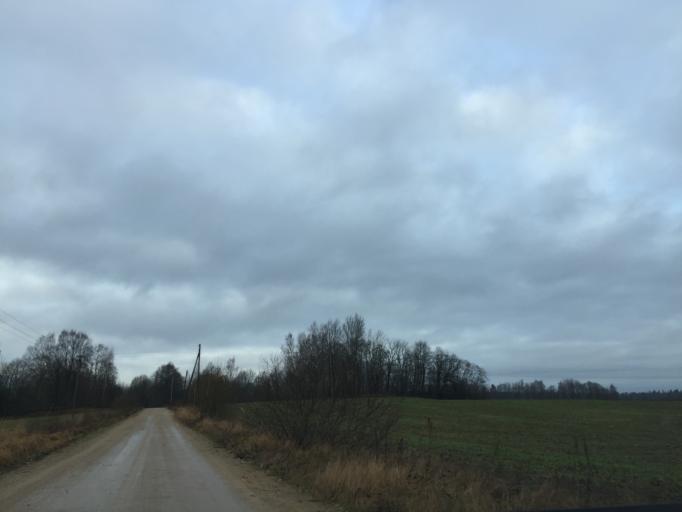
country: LV
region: Vainode
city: Vainode
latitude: 56.6106
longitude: 21.7971
